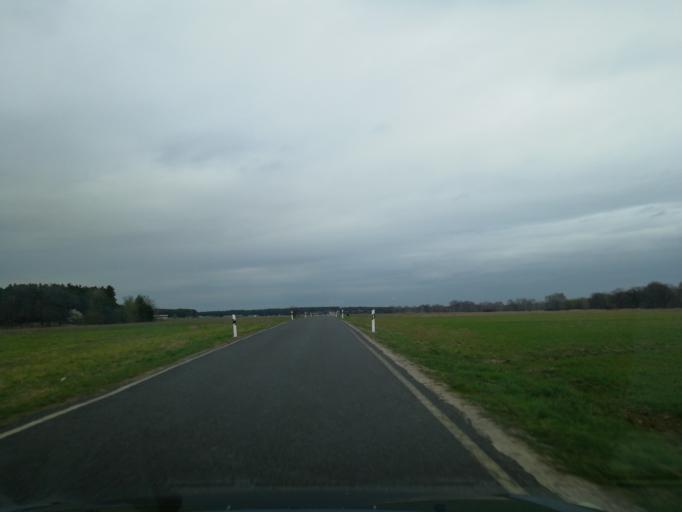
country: DE
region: Brandenburg
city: Calau
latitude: 51.7449
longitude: 14.0082
